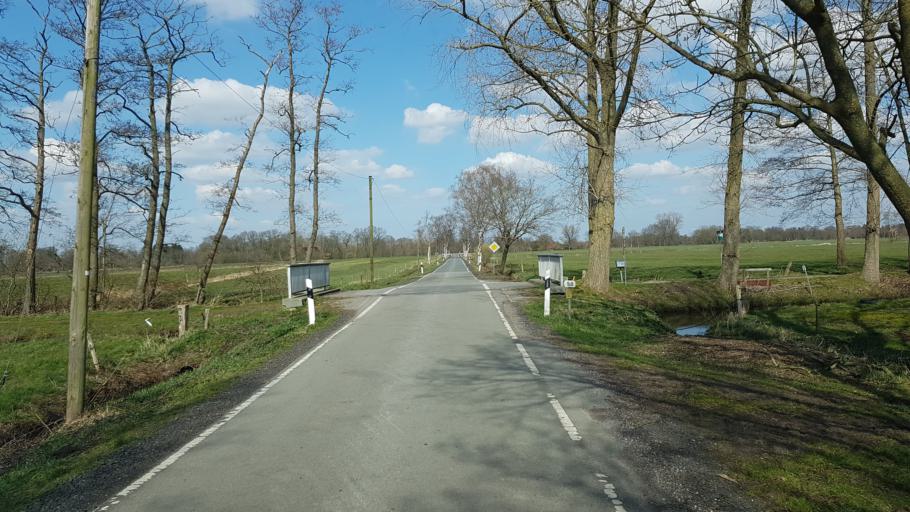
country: DE
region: Lower Saxony
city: Rastede
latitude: 53.3013
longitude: 8.2243
